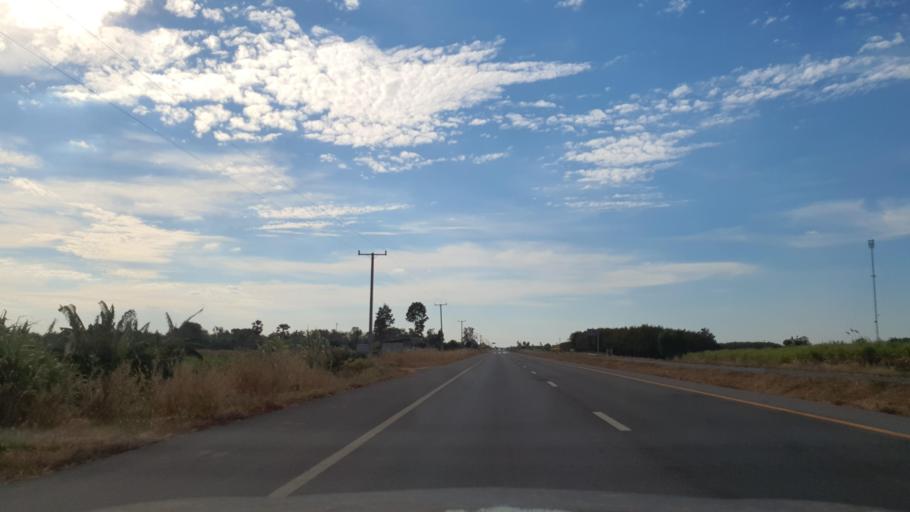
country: TH
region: Roi Et
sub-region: Amphoe Pho Chai
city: Pho Chai
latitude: 16.4150
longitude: 103.8071
